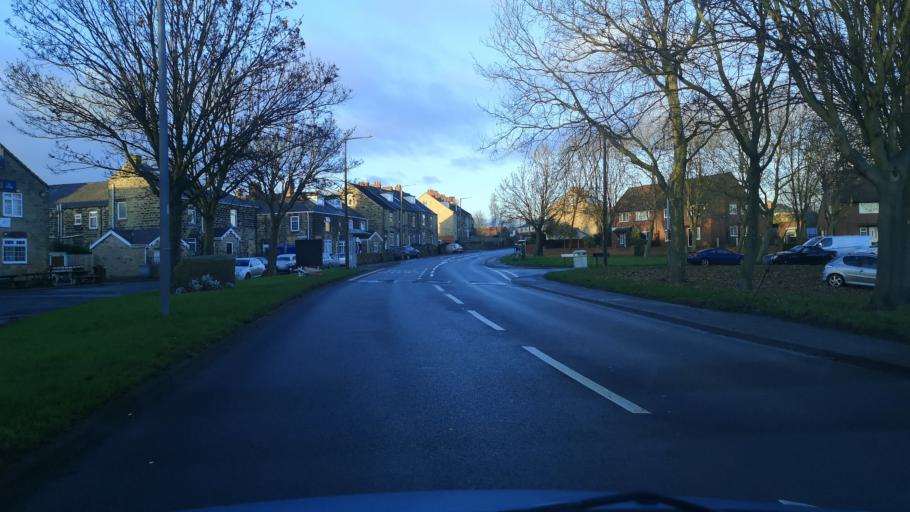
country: GB
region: England
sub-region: Barnsley
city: Great Houghton
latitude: 53.5493
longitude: -1.3468
